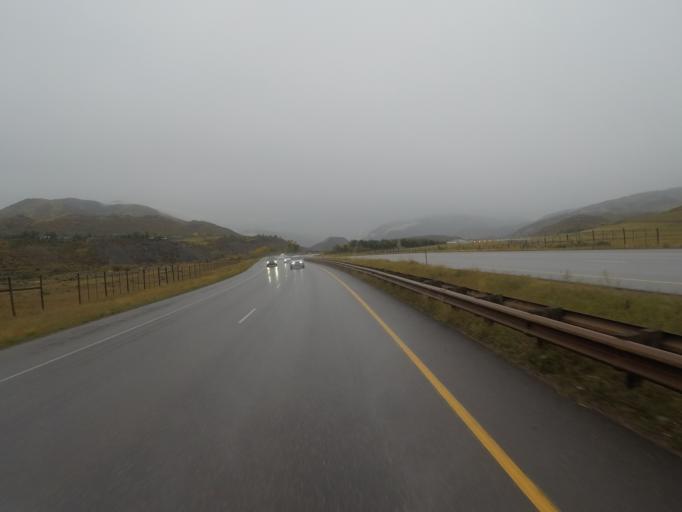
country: US
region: Colorado
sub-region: Pitkin County
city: Snowmass Village
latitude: 39.2365
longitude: -106.8750
